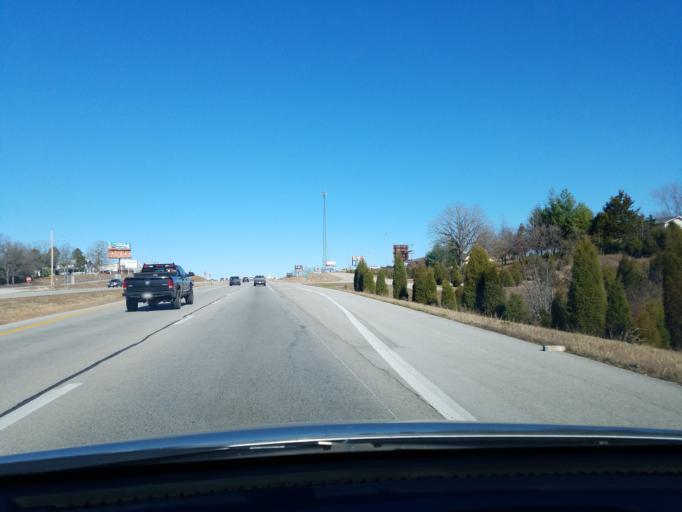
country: US
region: Missouri
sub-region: Taney County
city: Merriam Woods
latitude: 36.8034
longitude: -93.2256
